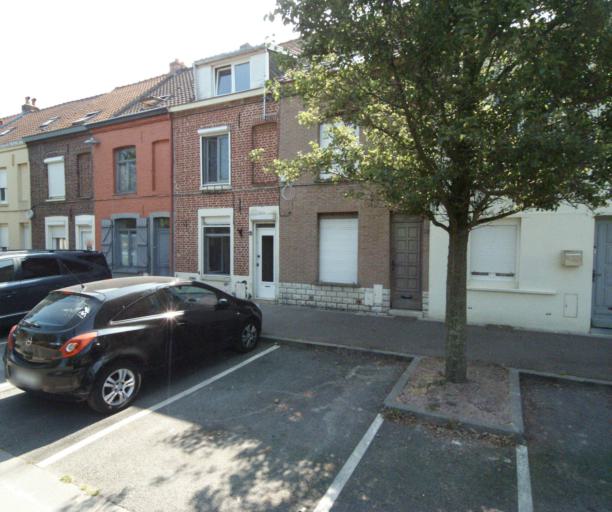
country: FR
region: Nord-Pas-de-Calais
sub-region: Departement du Nord
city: Tourcoing
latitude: 50.7282
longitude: 3.1536
